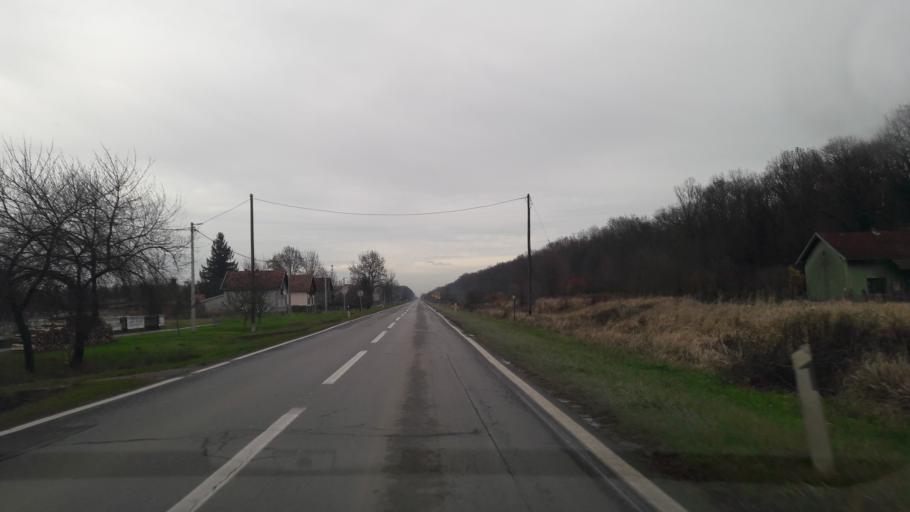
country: HR
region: Osjecko-Baranjska
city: Koska
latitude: 45.5581
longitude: 18.3679
